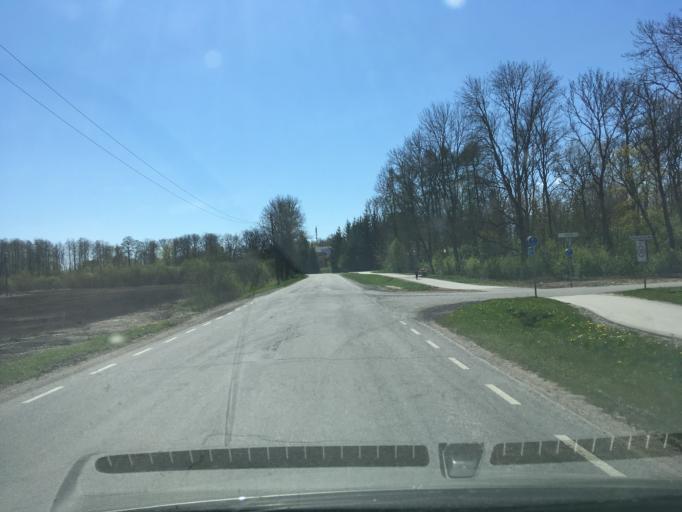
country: EE
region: Harju
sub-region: Raasiku vald
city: Arukula
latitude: 59.3622
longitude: 25.0825
